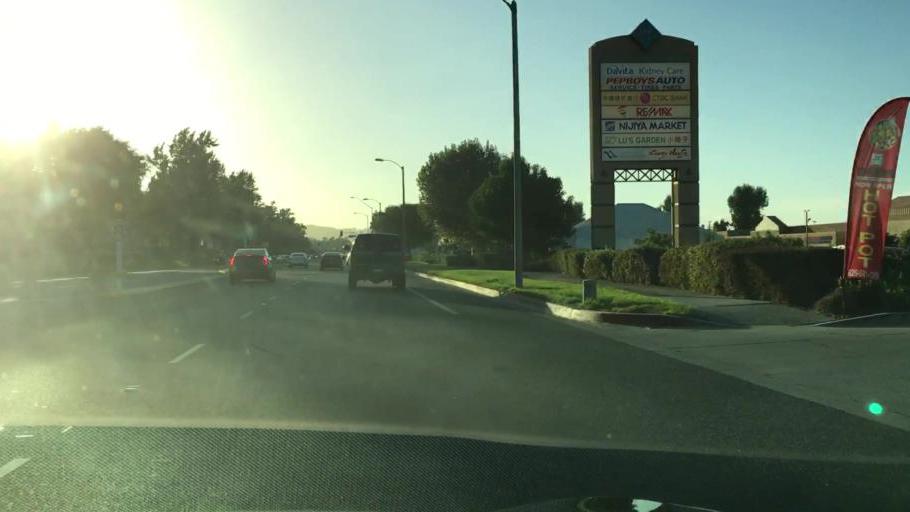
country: US
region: California
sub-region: Los Angeles County
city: Rowland Heights
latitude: 33.9901
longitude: -117.9156
